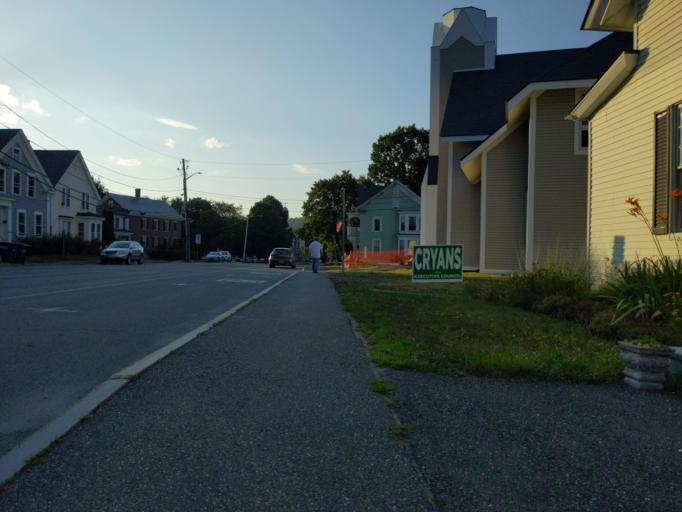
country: US
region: New Hampshire
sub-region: Grafton County
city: Lebanon
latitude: 43.6411
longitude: -72.2499
